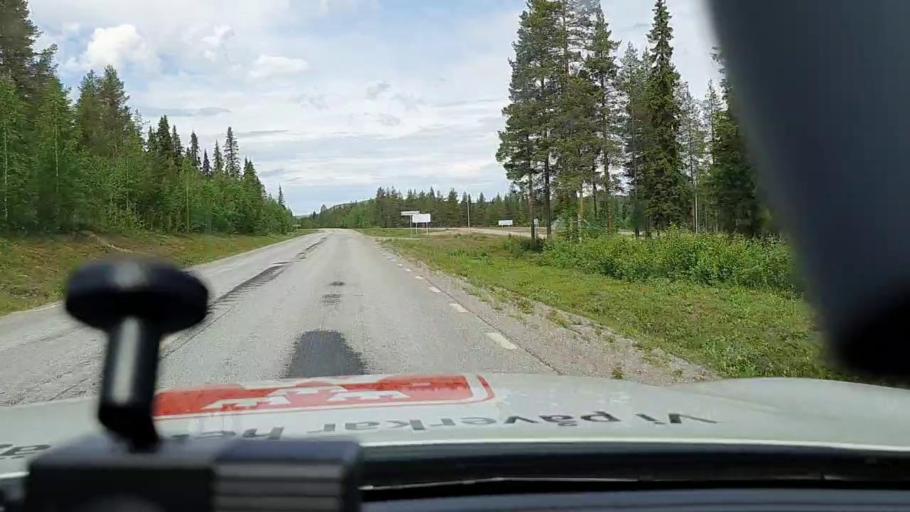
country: SE
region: Norrbotten
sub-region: Jokkmokks Kommun
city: Jokkmokk
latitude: 66.5524
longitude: 20.1165
